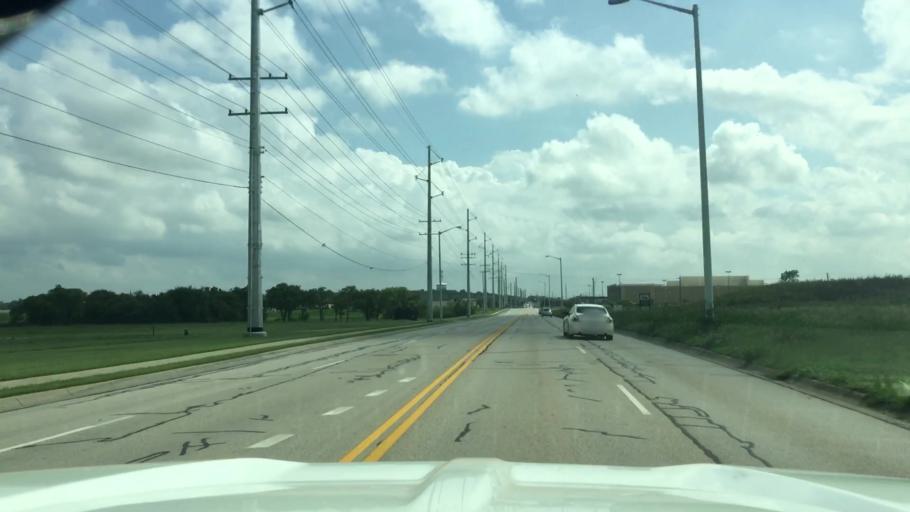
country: US
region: Texas
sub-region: Denton County
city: Denton
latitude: 33.2357
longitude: -97.1609
